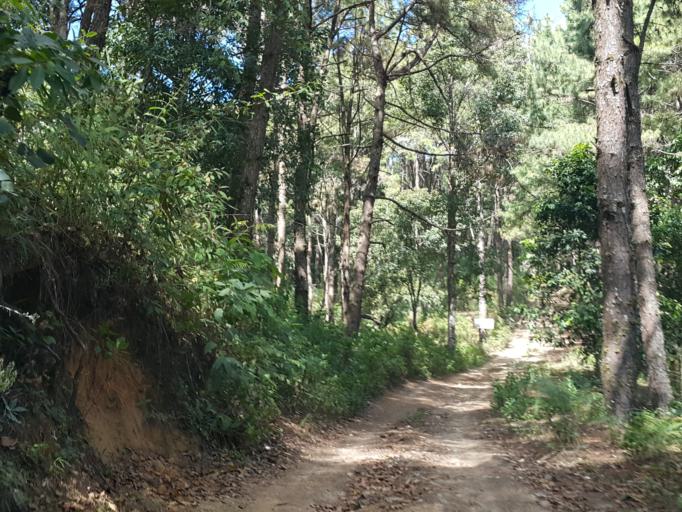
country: TH
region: Chiang Mai
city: Wiang Haeng
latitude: 19.5482
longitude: 98.8144
